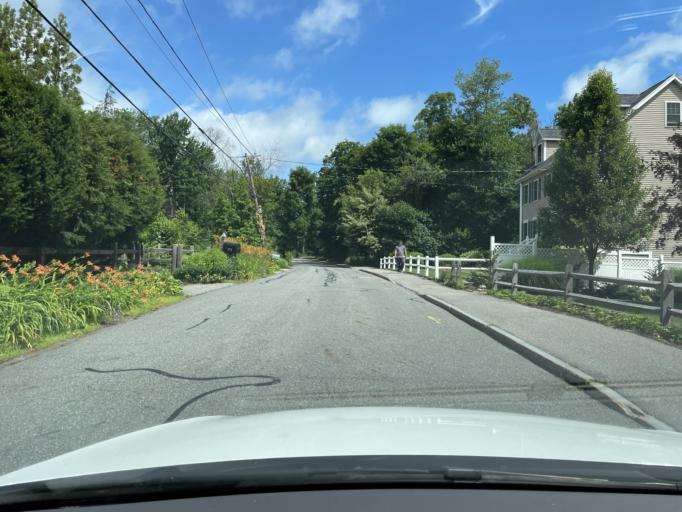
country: US
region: Massachusetts
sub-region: Essex County
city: Andover
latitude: 42.6327
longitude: -71.1212
